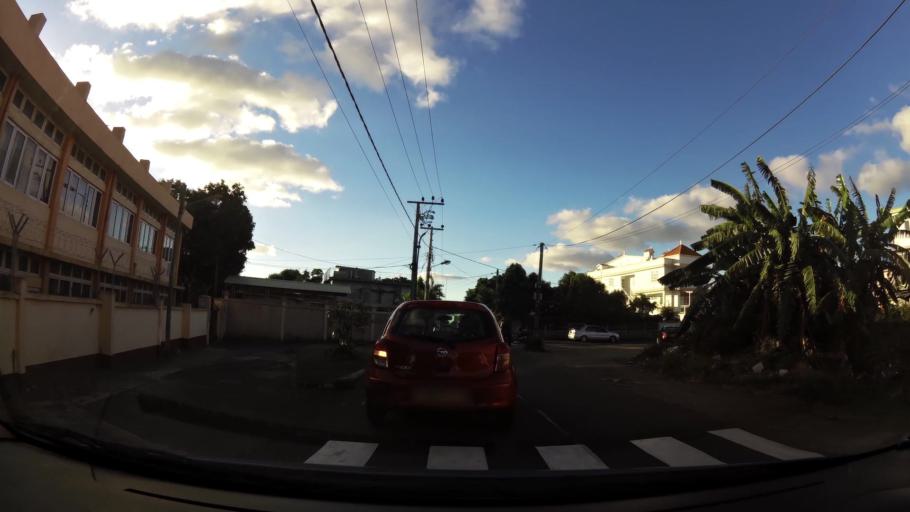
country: MU
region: Plaines Wilhems
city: Quatre Bornes
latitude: -20.2488
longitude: 57.4617
